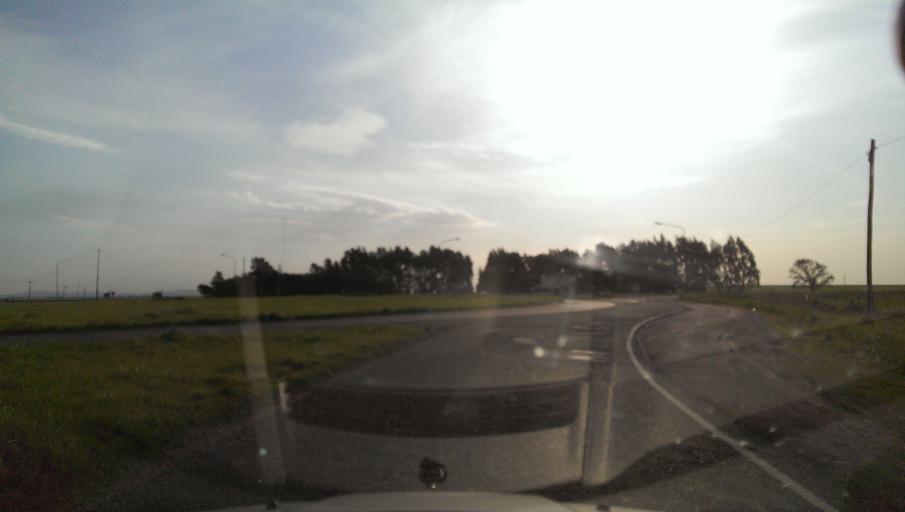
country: AR
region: Buenos Aires
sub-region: Partido de Coronel Suarez
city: Coronel Suarez
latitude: -37.7741
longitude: -61.7118
